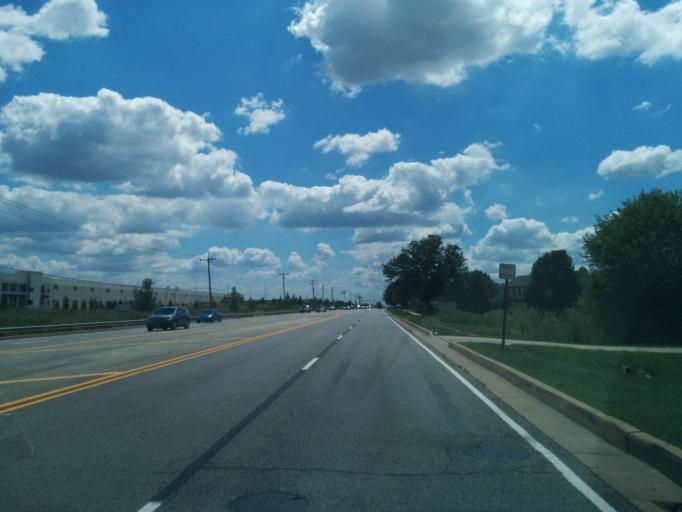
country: US
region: Illinois
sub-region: Will County
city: Romeoville
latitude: 41.6804
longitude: -88.1258
